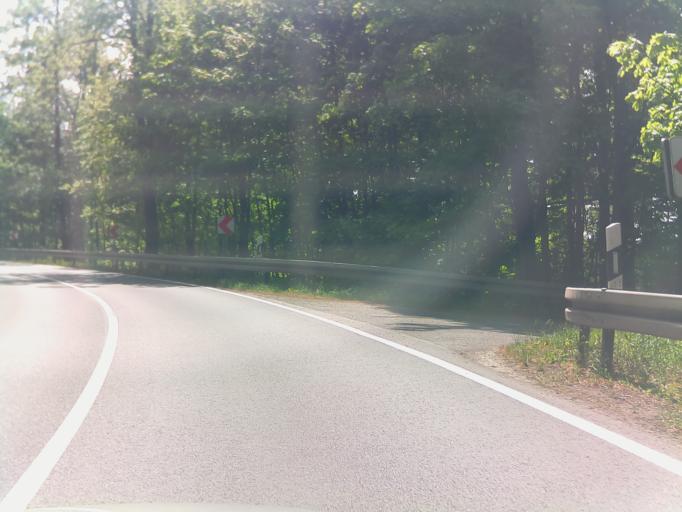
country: DE
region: Saxony-Anhalt
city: Huttenrode
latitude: 51.7260
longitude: 10.8918
